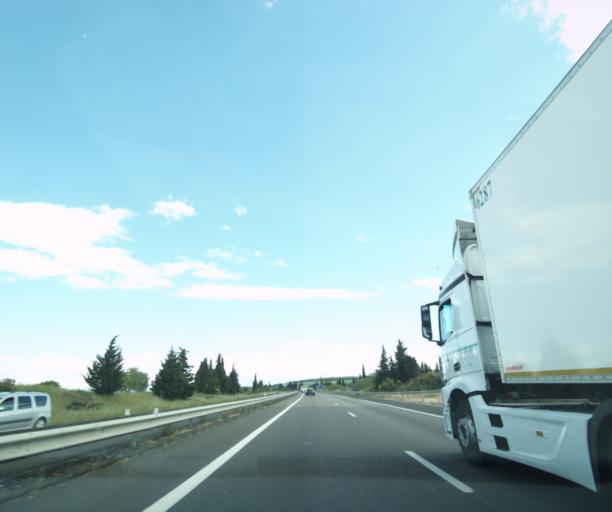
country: FR
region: Languedoc-Roussillon
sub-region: Departement du Gard
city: Garons
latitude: 43.7537
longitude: 4.4300
